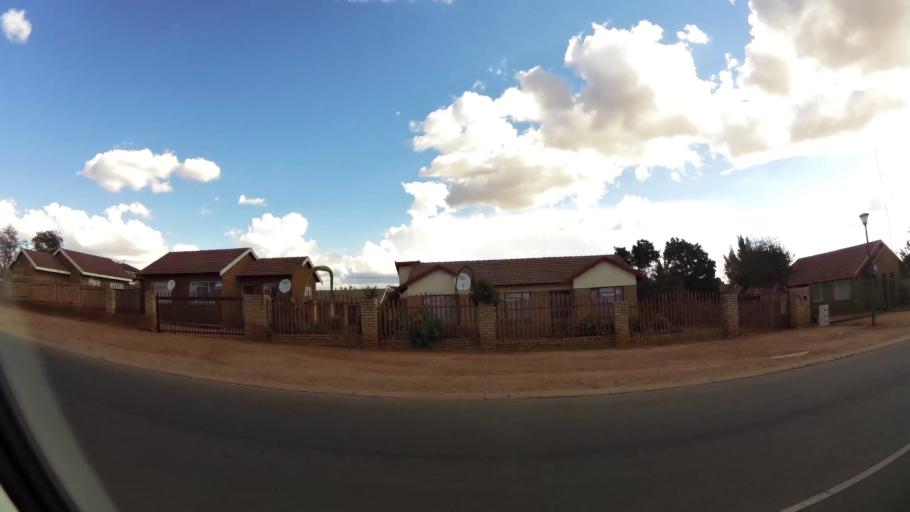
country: ZA
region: Limpopo
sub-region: Capricorn District Municipality
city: Polokwane
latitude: -23.9067
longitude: 29.5007
